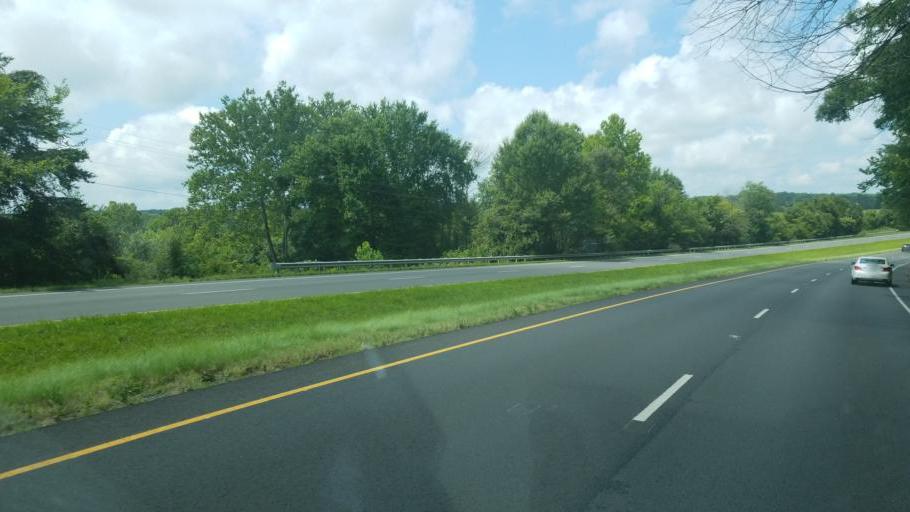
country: US
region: Virginia
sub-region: Fauquier County
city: Bealeton
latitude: 38.4670
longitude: -77.6770
